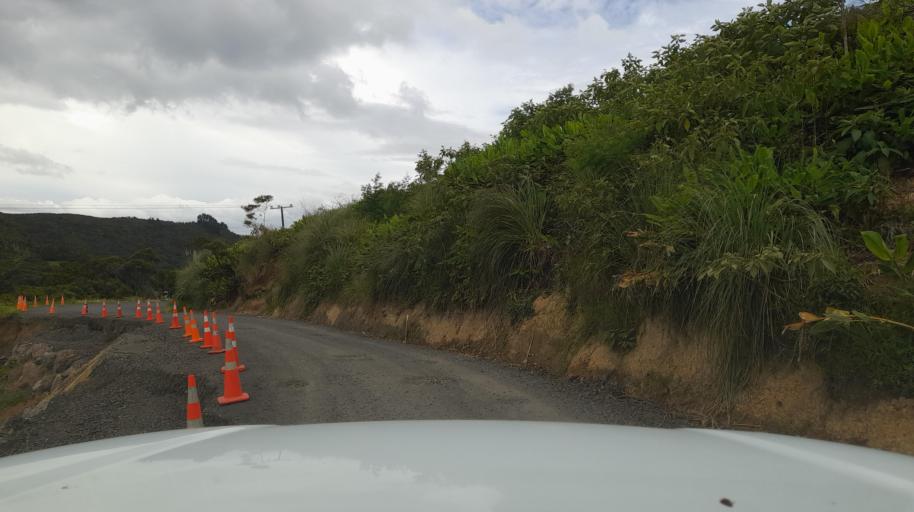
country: NZ
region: Northland
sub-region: Far North District
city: Kaitaia
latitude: -35.3747
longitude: 173.3801
